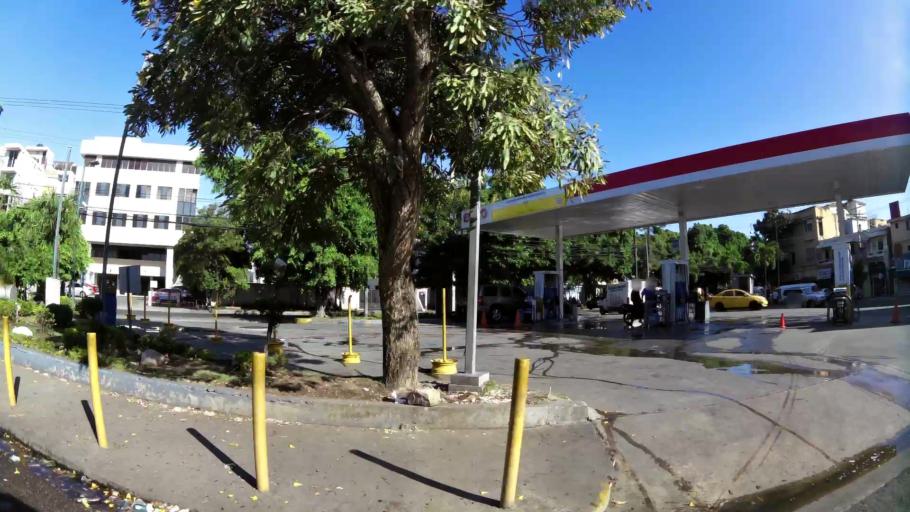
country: DO
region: Nacional
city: Ciudad Nueva
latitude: 18.4674
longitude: -69.8947
